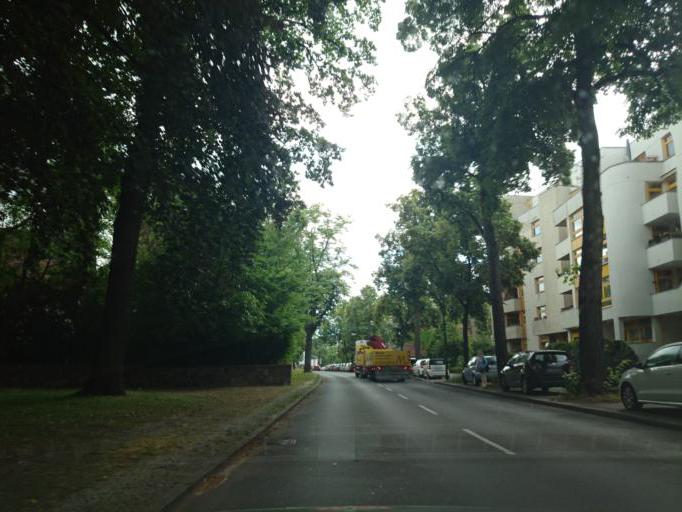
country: DE
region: Berlin
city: Lichterfelde
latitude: 52.4374
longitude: 13.3147
